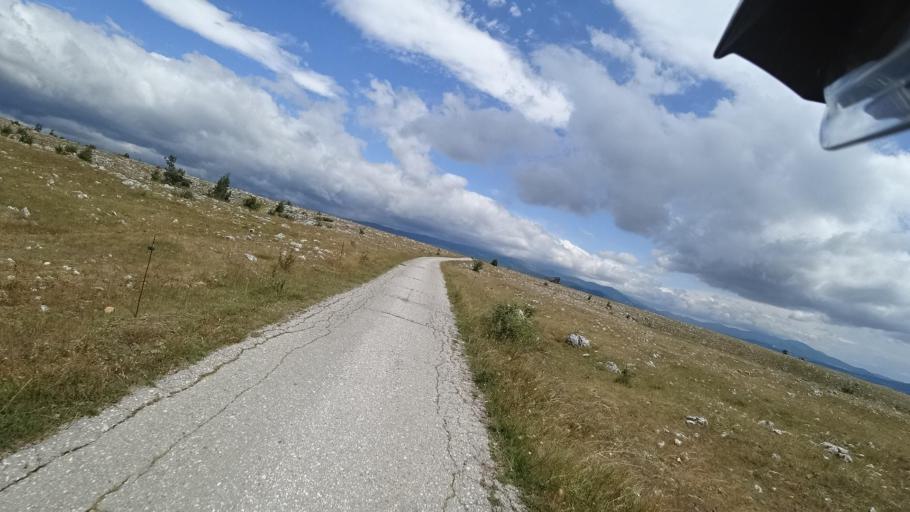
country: HR
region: Licko-Senjska
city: Jezerce
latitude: 44.6153
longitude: 15.6486
